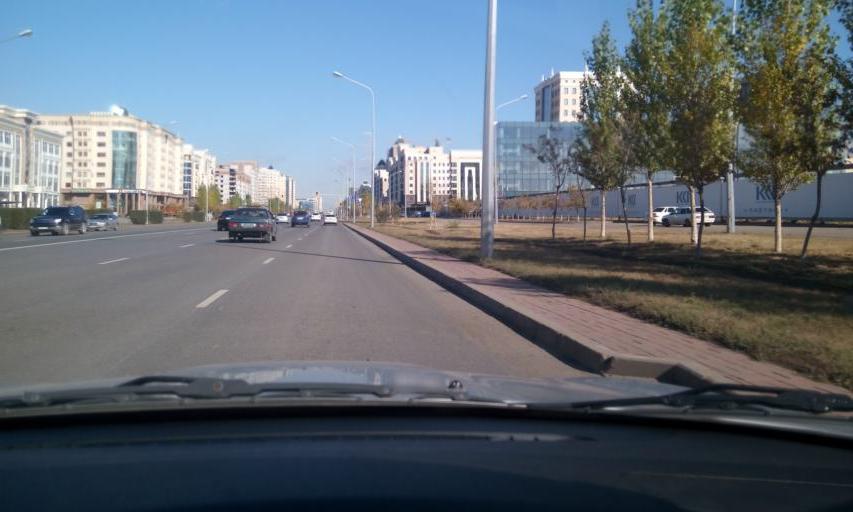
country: KZ
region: Astana Qalasy
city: Astana
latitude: 51.1067
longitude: 71.4311
